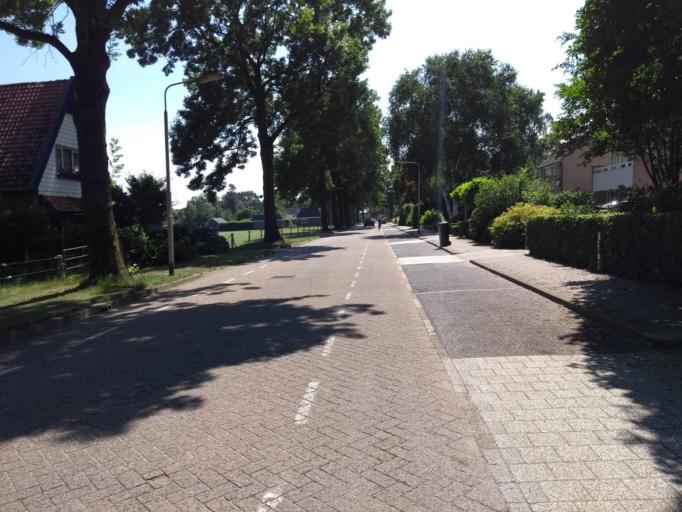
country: NL
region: Overijssel
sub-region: Gemeente Wierden
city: Wierden
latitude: 52.3593
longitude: 6.6096
